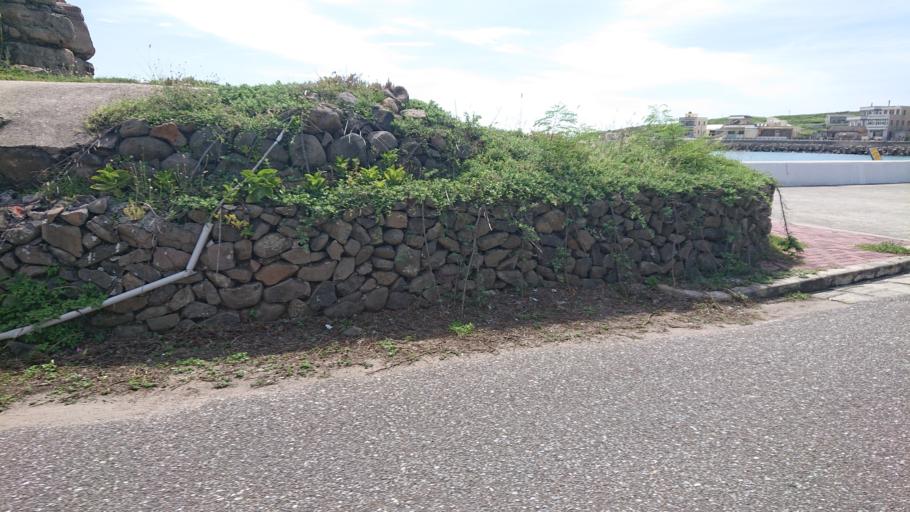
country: TW
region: Taiwan
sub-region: Penghu
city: Ma-kung
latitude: 23.6511
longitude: 119.5179
